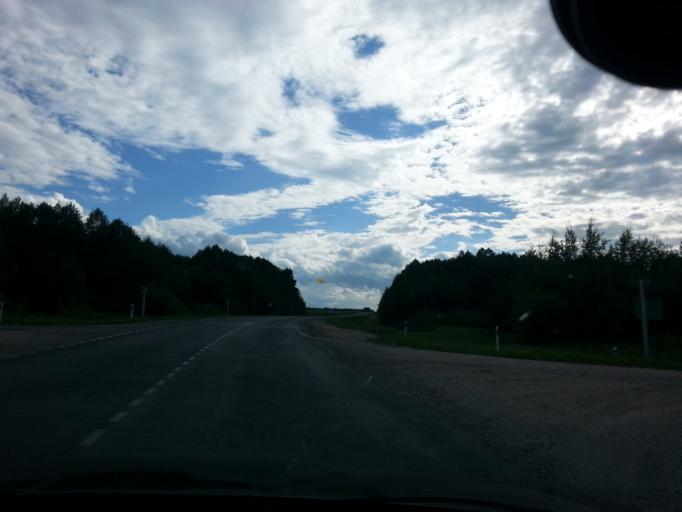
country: BY
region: Grodnenskaya
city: Astravyets
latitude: 54.8017
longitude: 26.1271
